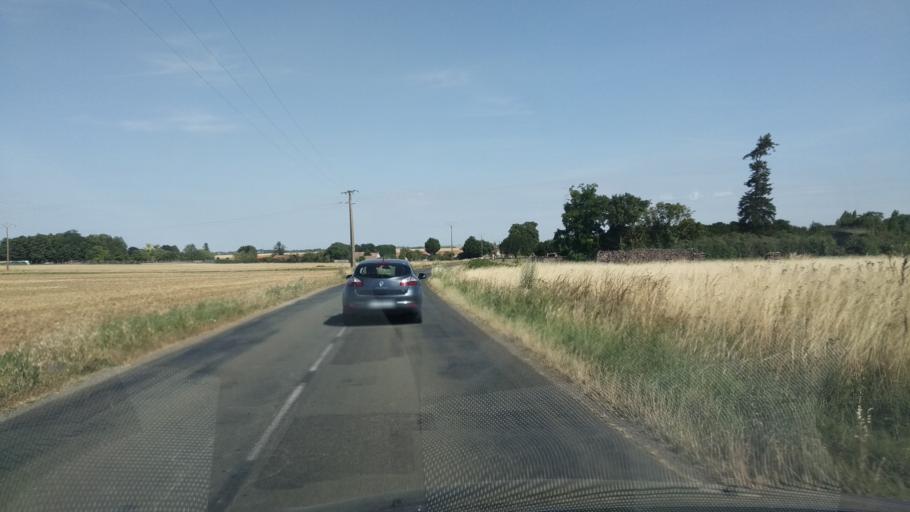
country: FR
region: Poitou-Charentes
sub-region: Departement de la Vienne
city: Vouille
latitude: 46.6815
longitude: 0.1737
